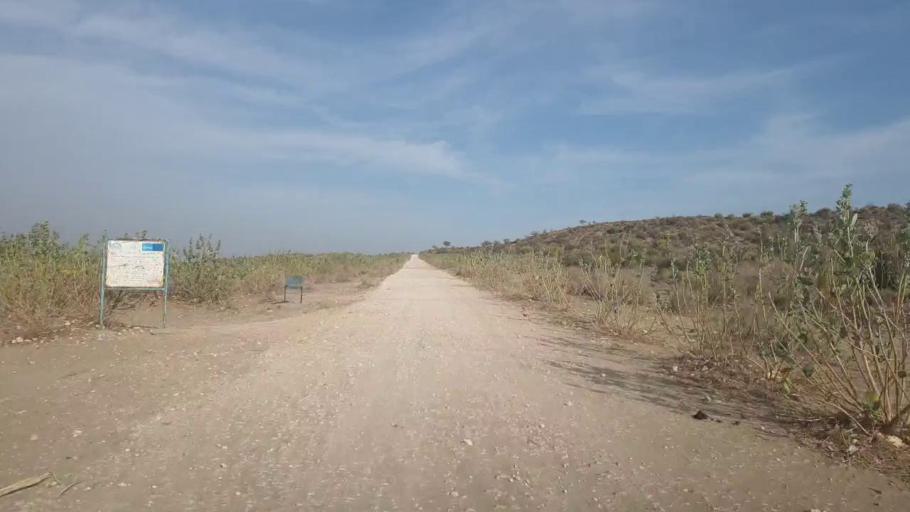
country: PK
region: Sindh
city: Nabisar
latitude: 25.0524
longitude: 69.7093
